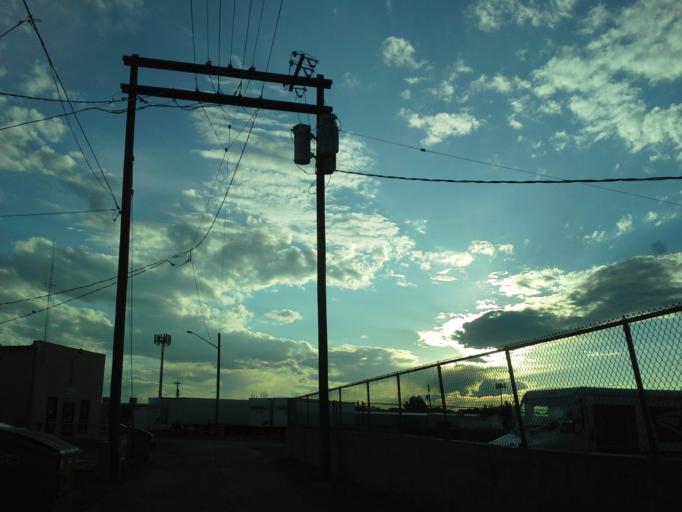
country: US
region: Wyoming
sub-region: Washakie County
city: Worland
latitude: 44.0174
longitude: -107.9609
